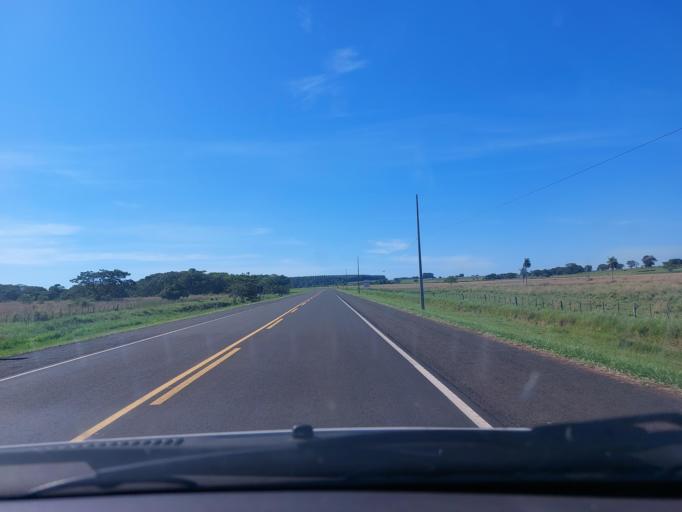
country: PY
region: San Pedro
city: Itacurubi del Rosario
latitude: -24.6030
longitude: -56.7799
